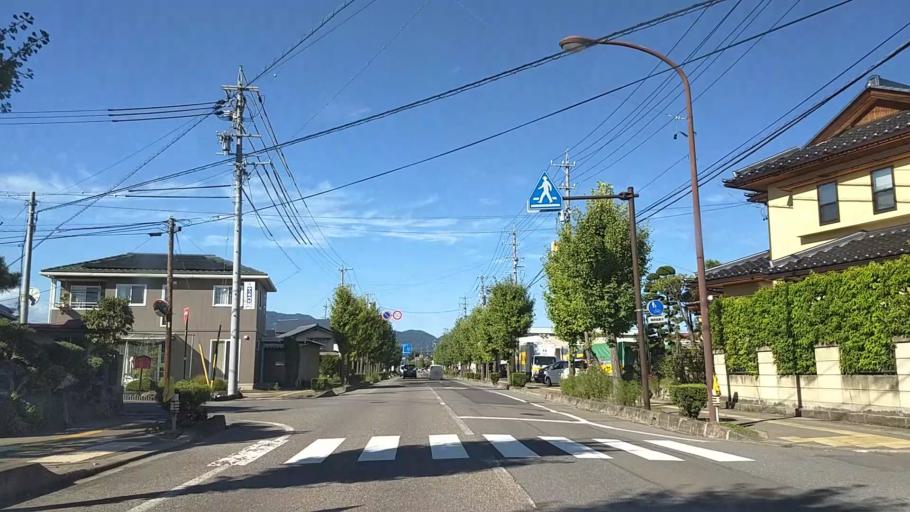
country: JP
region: Nagano
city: Nagano-shi
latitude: 36.5805
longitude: 138.1359
